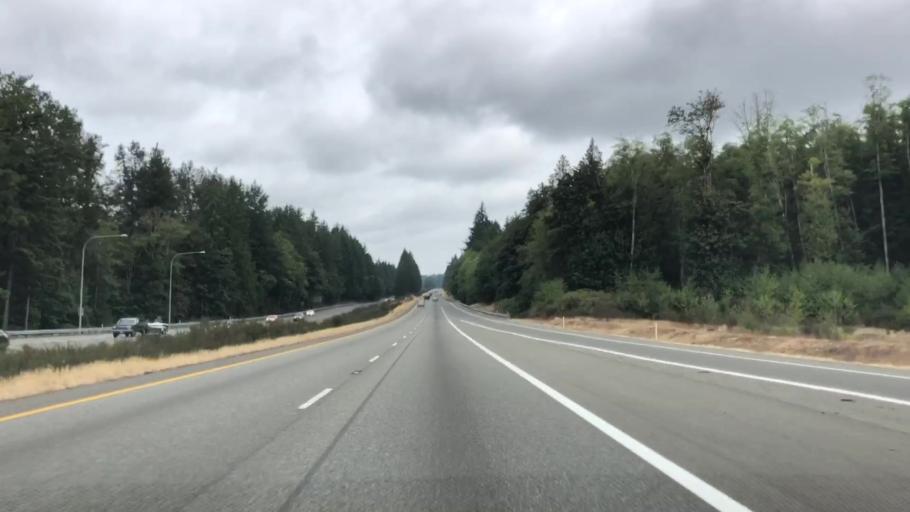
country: US
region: Washington
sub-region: Kitsap County
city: Burley
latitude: 47.4347
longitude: -122.6228
